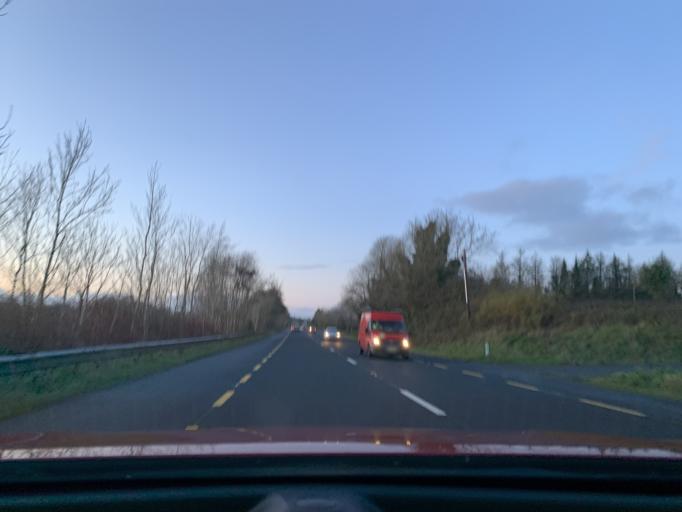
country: IE
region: Connaught
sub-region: County Leitrim
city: Carrick-on-Shannon
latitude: 53.9076
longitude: -7.9625
